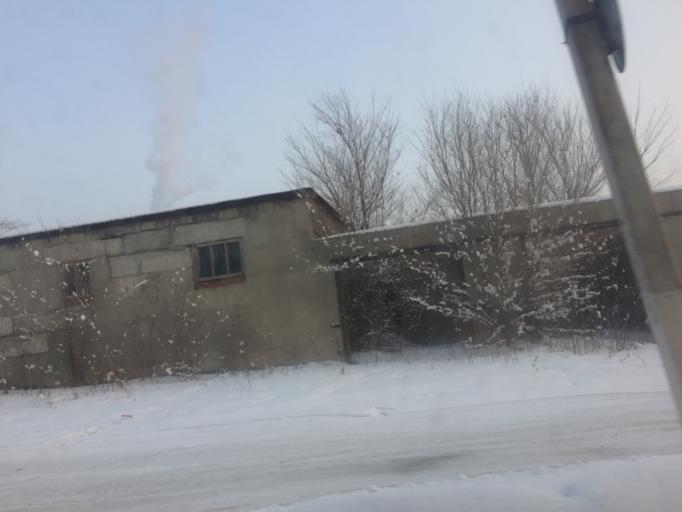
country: RU
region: Chelyabinsk
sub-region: Gorod Magnitogorsk
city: Magnitogorsk
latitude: 53.4654
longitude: 59.0716
